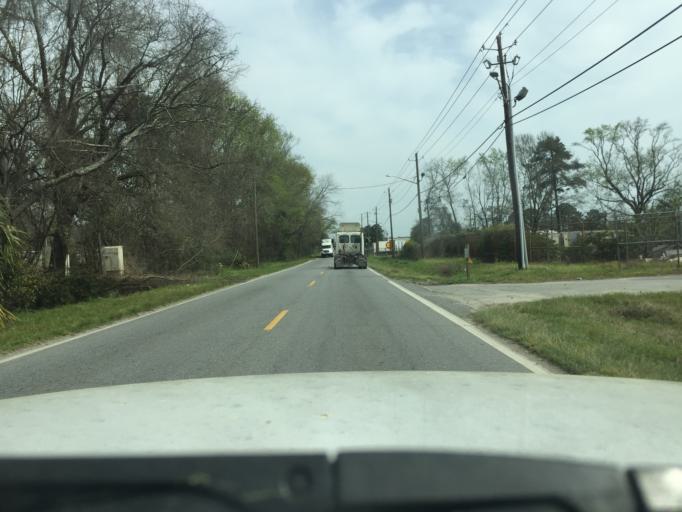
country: US
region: Georgia
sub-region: Chatham County
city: Savannah
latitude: 32.0816
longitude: -81.1212
